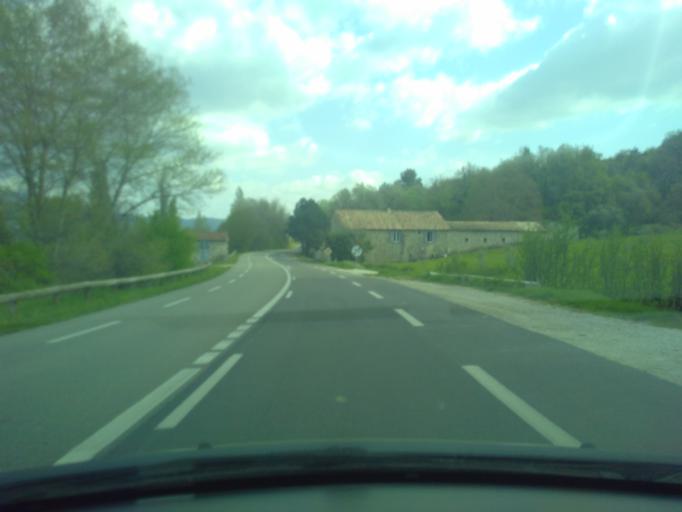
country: FR
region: Provence-Alpes-Cote d'Azur
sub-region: Departement du Vaucluse
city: Vaison-la-Romaine
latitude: 44.2108
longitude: 5.1014
